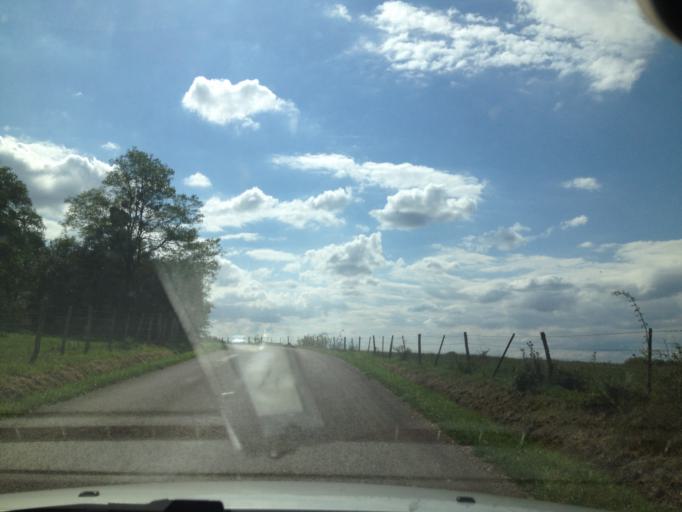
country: FR
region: Franche-Comte
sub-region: Departement de la Haute-Saone
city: Saint-Loup-sur-Semouse
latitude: 47.9316
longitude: 6.1553
